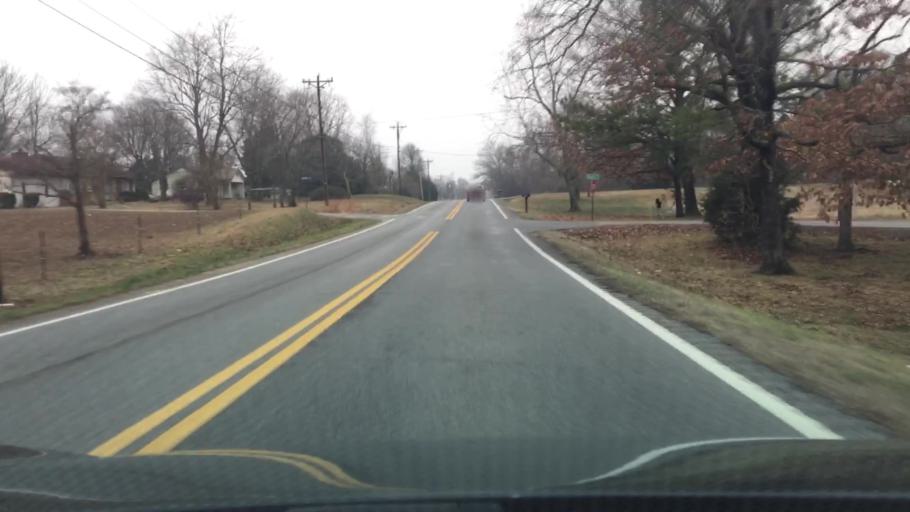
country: US
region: Kentucky
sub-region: Livingston County
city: Ledbetter
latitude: 36.9686
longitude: -88.4247
